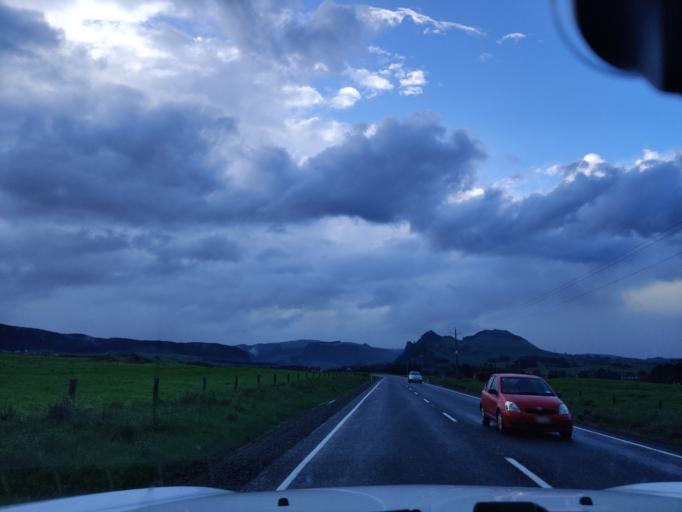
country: NZ
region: Waikato
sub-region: South Waikato District
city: Tokoroa
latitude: -38.4044
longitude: 175.7913
